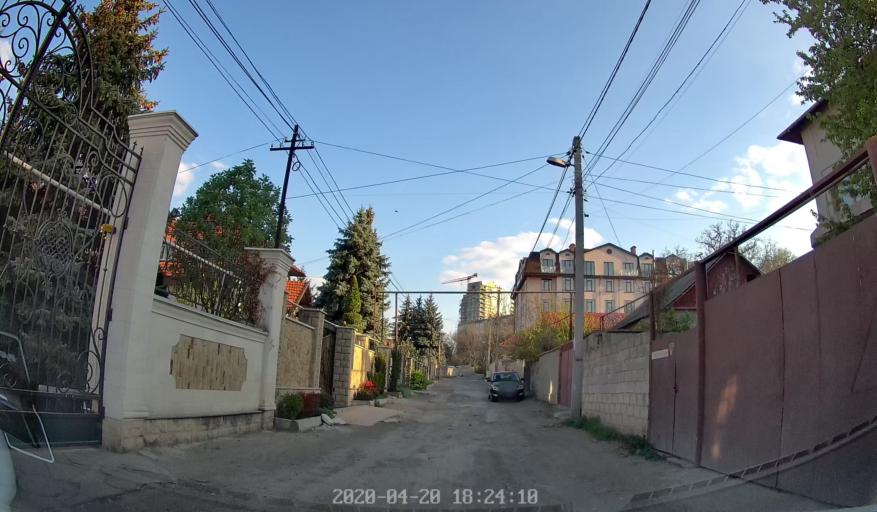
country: MD
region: Chisinau
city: Chisinau
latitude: 46.9946
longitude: 28.8378
